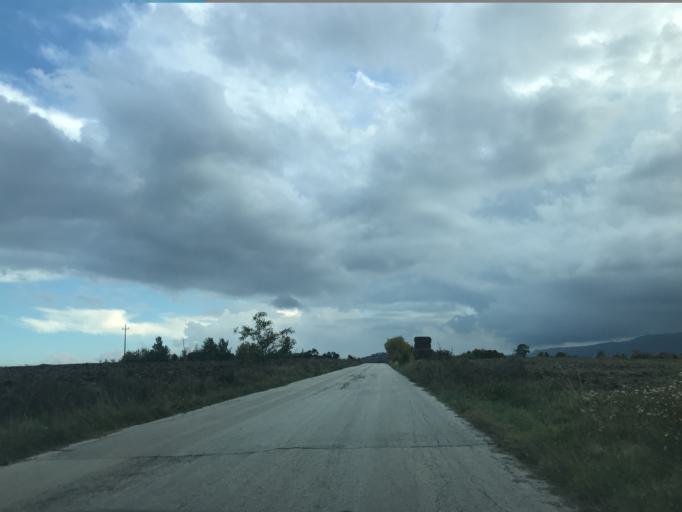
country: IT
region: Molise
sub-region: Provincia di Isernia
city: Bagnoli del Trigno
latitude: 41.6907
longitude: 14.4621
